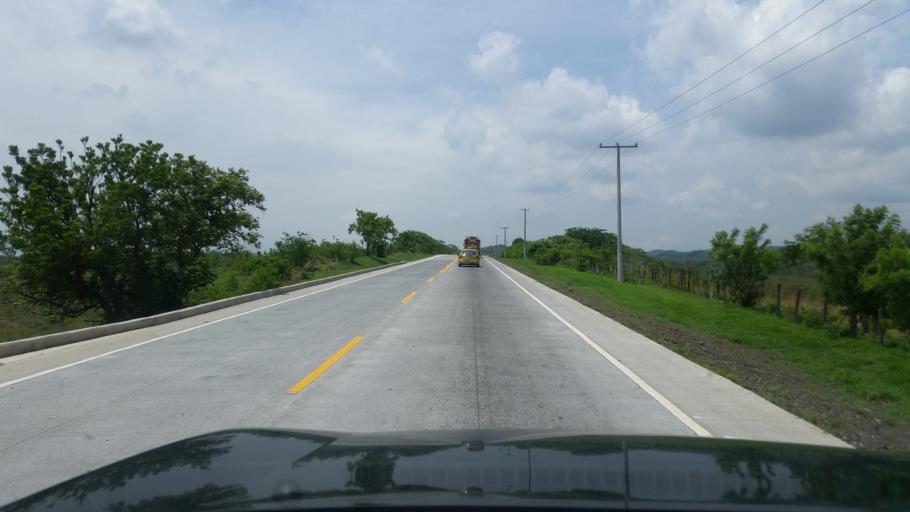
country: NI
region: Managua
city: Carlos Fonseca Amador
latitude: 12.0716
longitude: -86.4351
